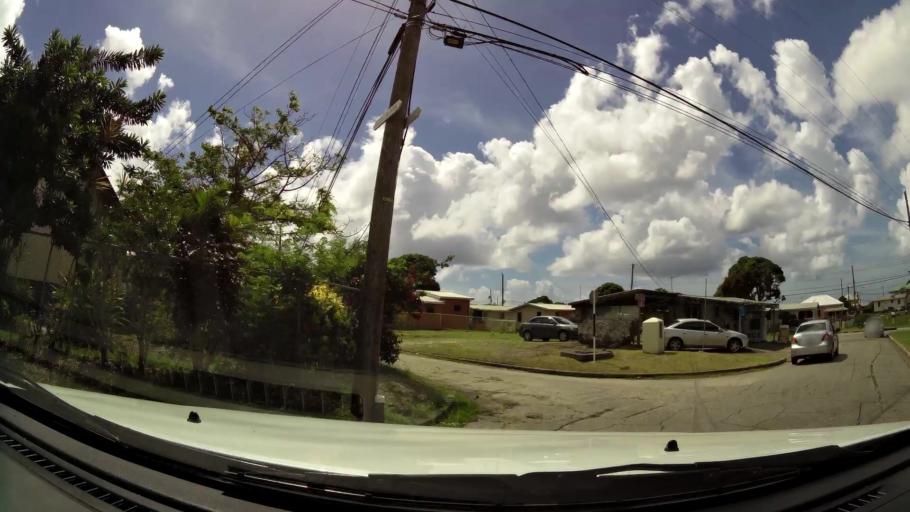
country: BB
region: Saint James
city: Holetown
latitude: 13.1508
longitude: -59.6257
